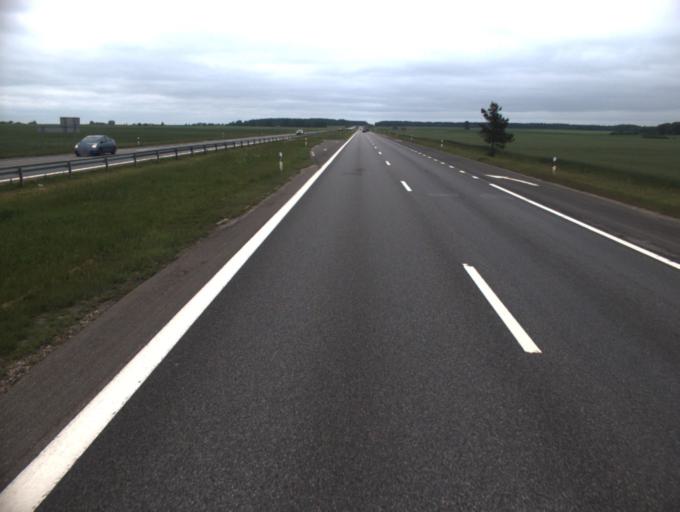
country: LT
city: Ariogala
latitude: 55.2743
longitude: 23.3689
